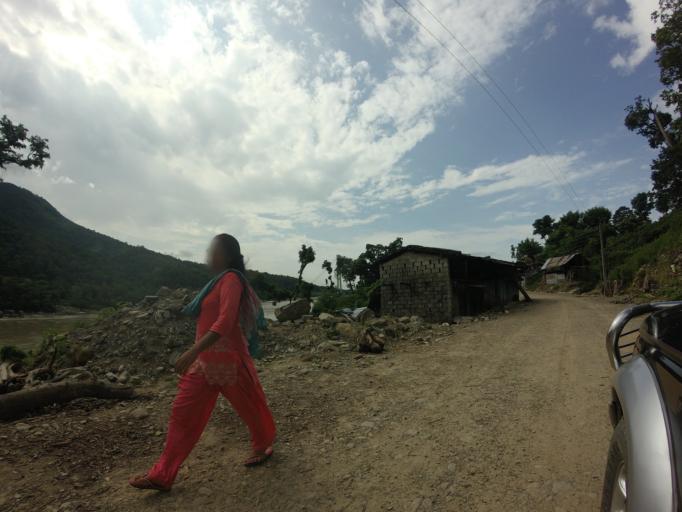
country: NP
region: Far Western
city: Tikapur
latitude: 28.6486
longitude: 81.2858
